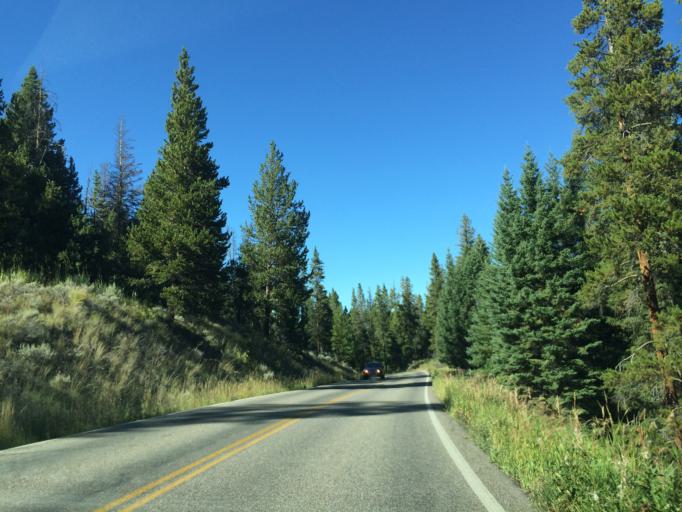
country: US
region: Montana
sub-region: Gallatin County
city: West Yellowstone
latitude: 44.8814
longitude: -110.3820
